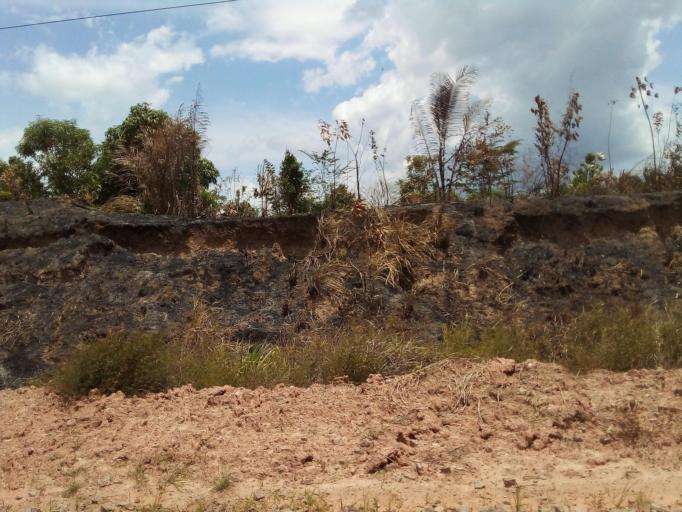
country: BR
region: Maranhao
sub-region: Itapecuru Mirim
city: Itapecuru Mirim
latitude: -3.1429
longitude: -44.3420
